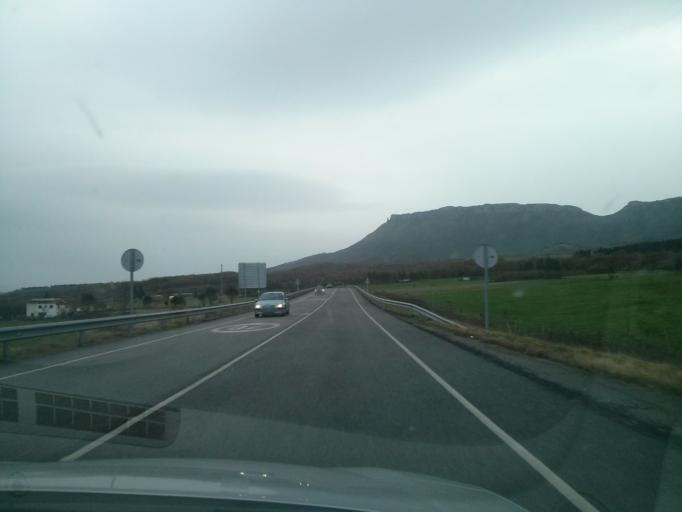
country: ES
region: Castille and Leon
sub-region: Provincia de Burgos
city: Villasana de Mena
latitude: 43.0939
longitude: -3.2872
